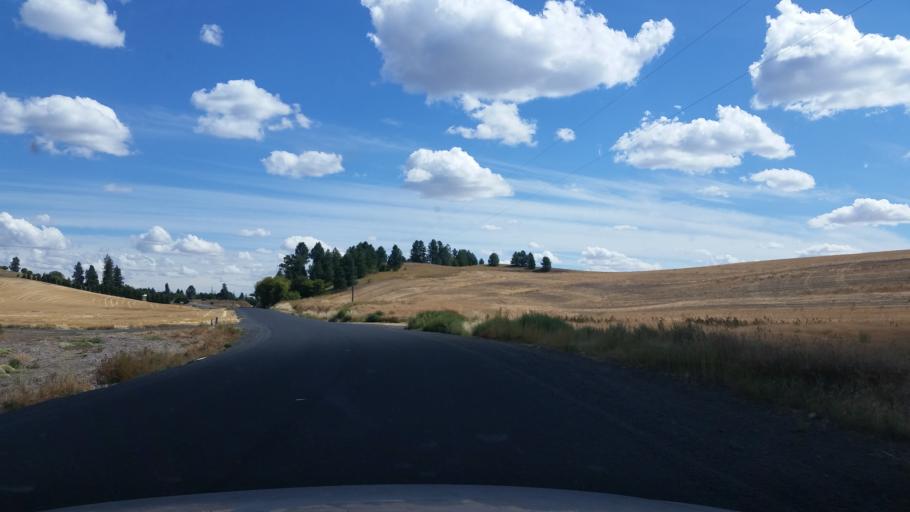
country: US
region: Washington
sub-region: Spokane County
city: Cheney
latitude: 47.4834
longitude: -117.6126
